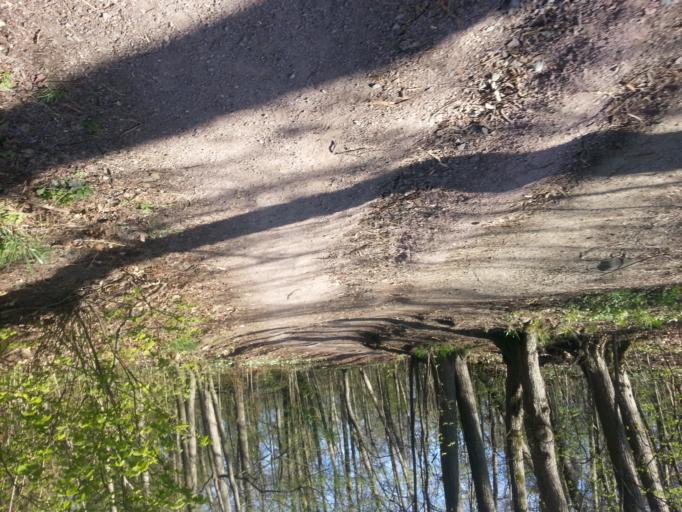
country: NO
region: Oslo
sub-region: Oslo
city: Sjolyststranda
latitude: 59.9166
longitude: 10.6865
